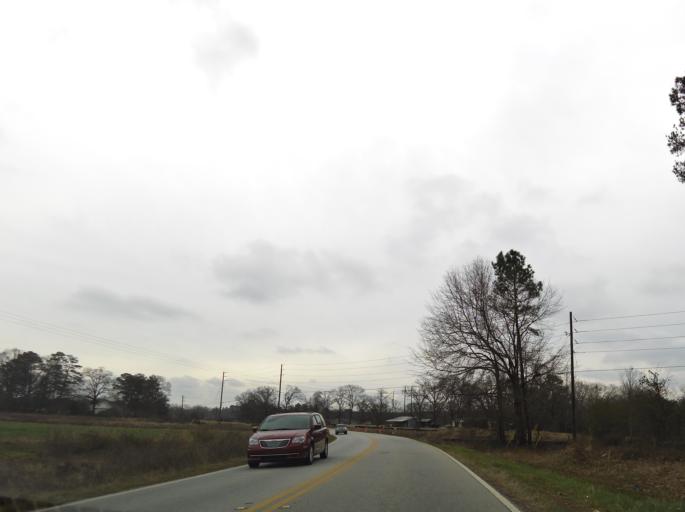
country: US
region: Georgia
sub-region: Houston County
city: Robins Air Force Base
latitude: 32.5526
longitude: -83.5845
